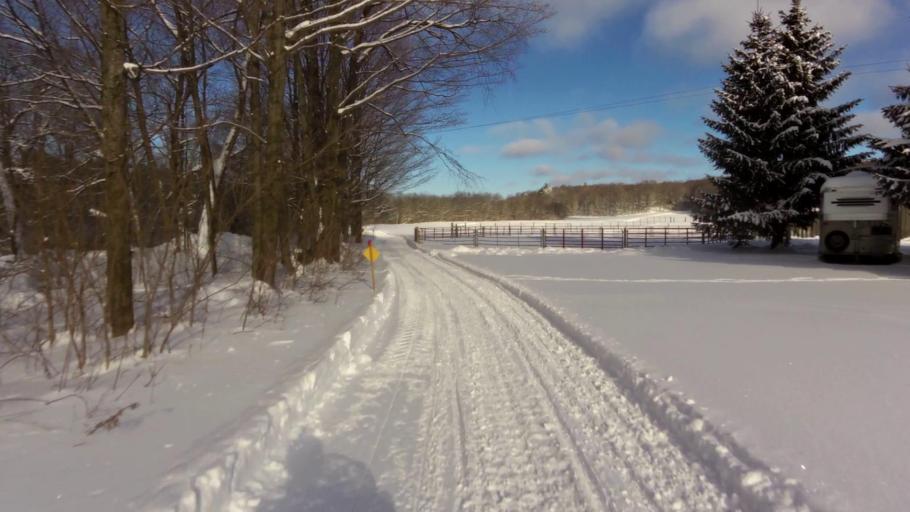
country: US
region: New York
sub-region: Chautauqua County
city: Falconer
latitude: 42.2491
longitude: -79.1423
